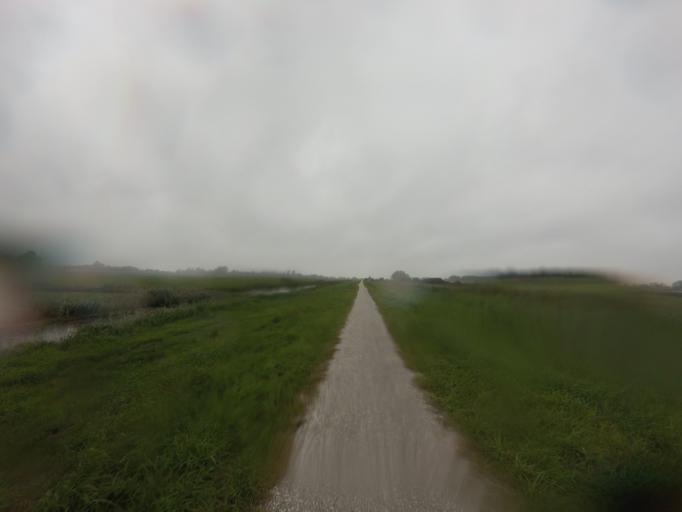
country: NL
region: Friesland
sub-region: Gemeente Smallingerland
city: Oudega
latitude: 53.1022
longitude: 5.9646
